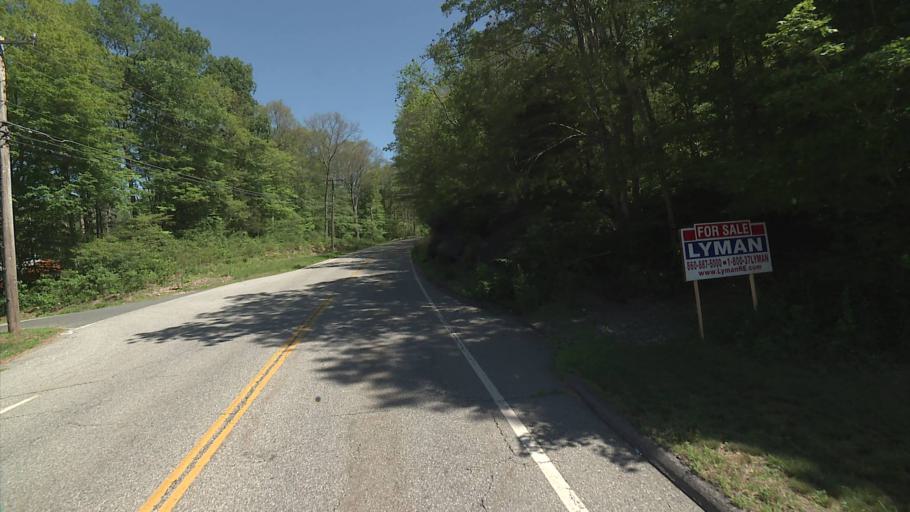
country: US
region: Connecticut
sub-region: Windham County
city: Willimantic
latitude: 41.6577
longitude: -72.2276
